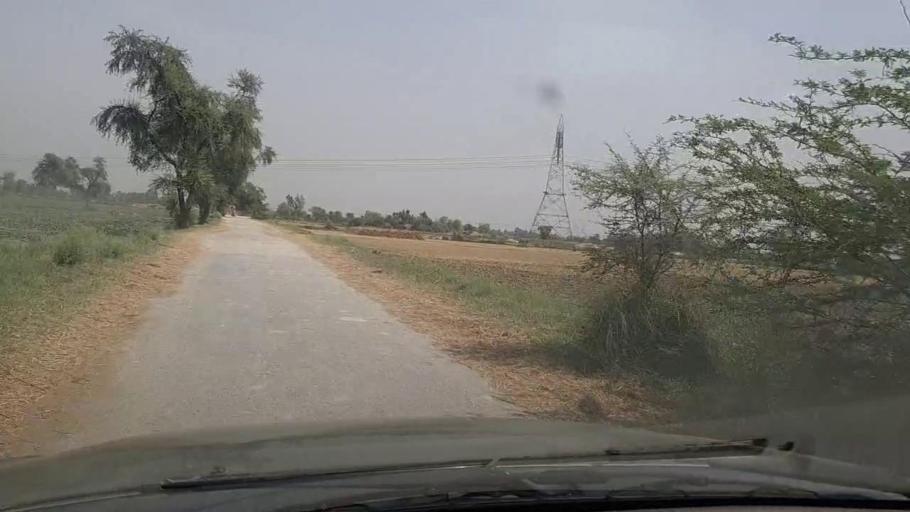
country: PK
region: Sindh
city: Shikarpur
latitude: 27.9209
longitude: 68.6767
